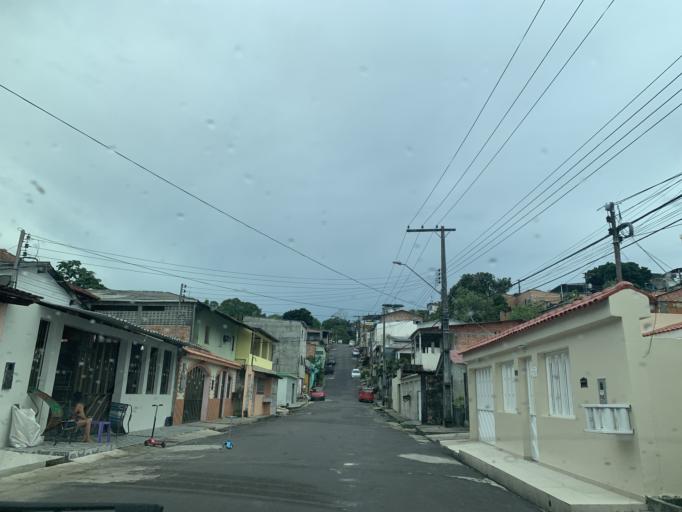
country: BR
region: Amazonas
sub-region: Manaus
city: Manaus
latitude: -3.0849
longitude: -59.9731
